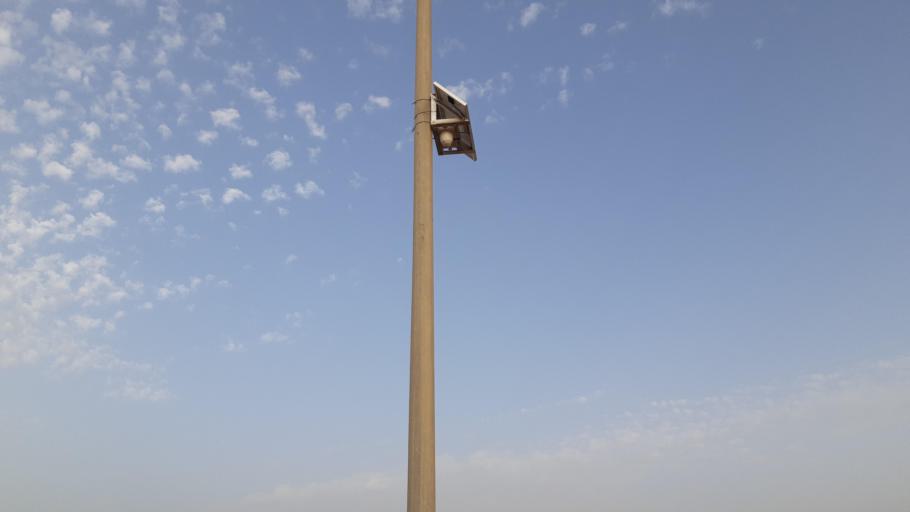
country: TN
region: Madanin
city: Zarzis
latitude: 33.6093
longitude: 10.9899
